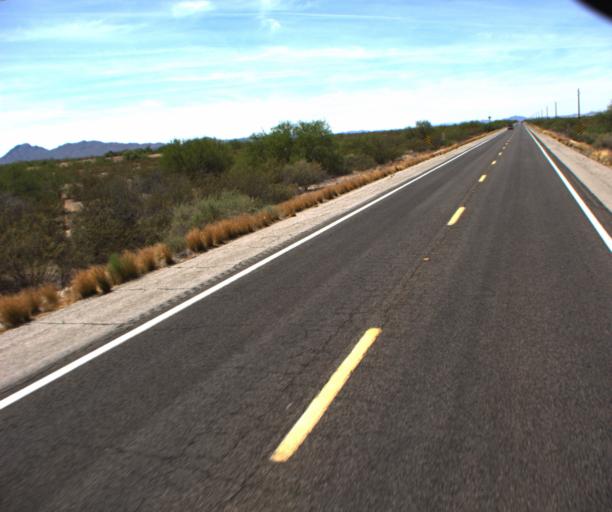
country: US
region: Arizona
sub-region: La Paz County
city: Salome
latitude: 33.8679
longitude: -113.4002
